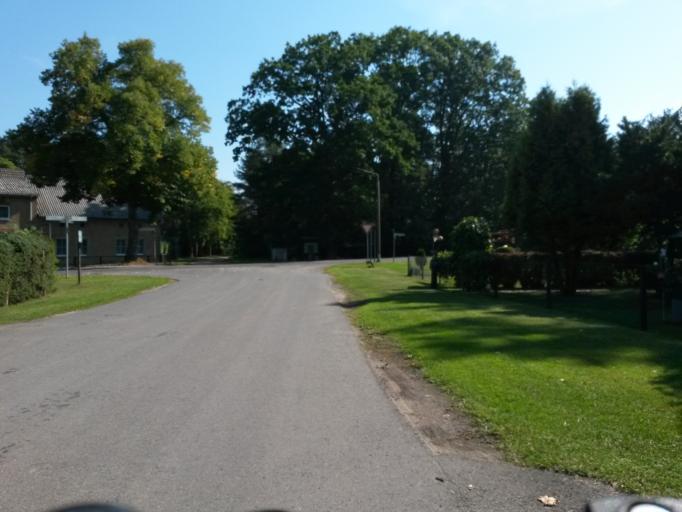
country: DE
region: Brandenburg
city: Zehdenick
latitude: 53.0336
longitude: 13.3853
